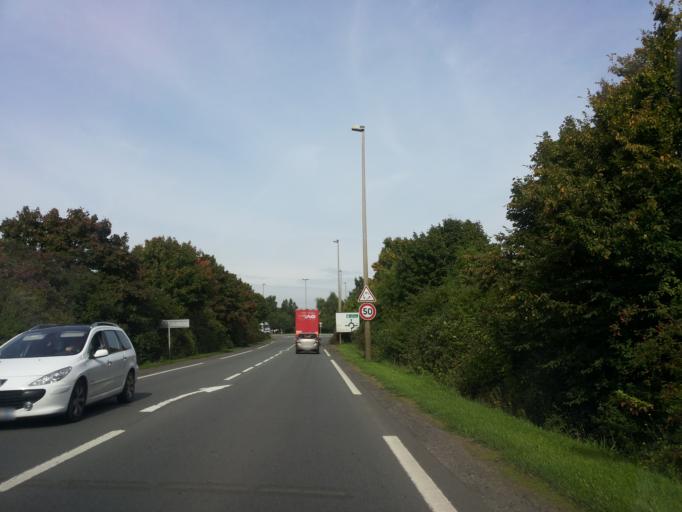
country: FR
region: Nord-Pas-de-Calais
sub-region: Departement du Pas-de-Calais
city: Saint-Laurent-Blangy
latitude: 50.2862
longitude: 2.8032
